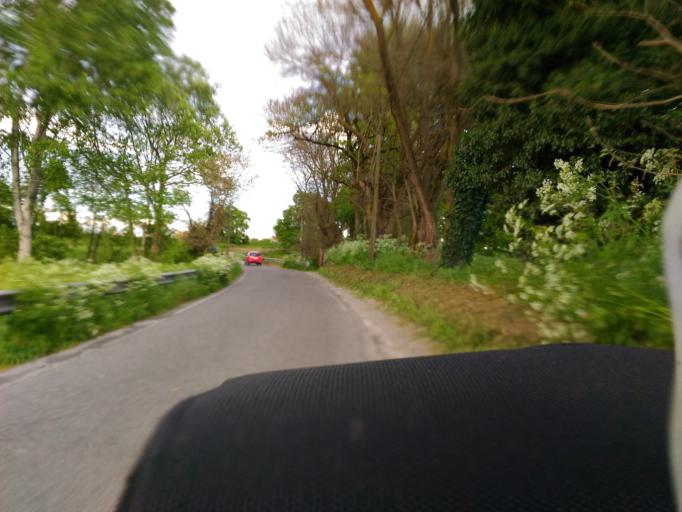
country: IT
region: Lombardy
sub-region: Citta metropolitana di Milano
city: Triginto
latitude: 45.4000
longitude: 9.3160
